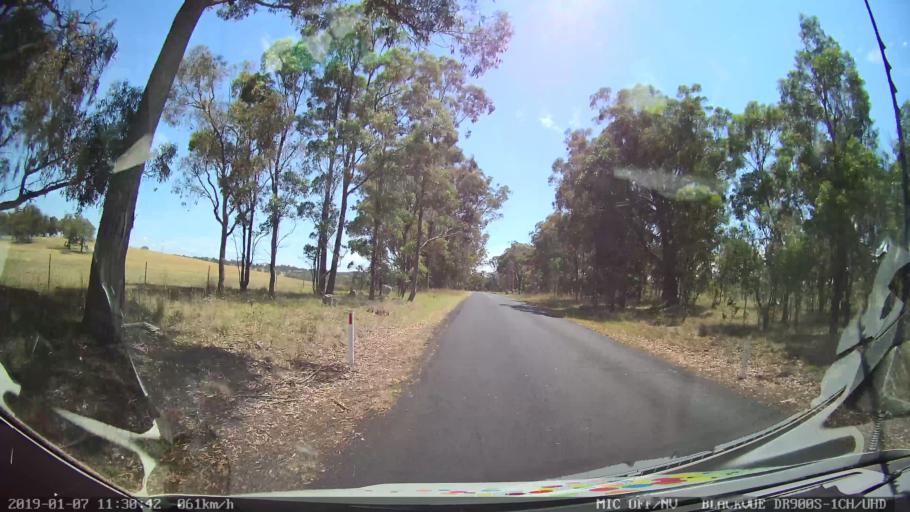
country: AU
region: New South Wales
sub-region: Armidale Dumaresq
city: Armidale
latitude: -30.4267
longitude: 151.5633
